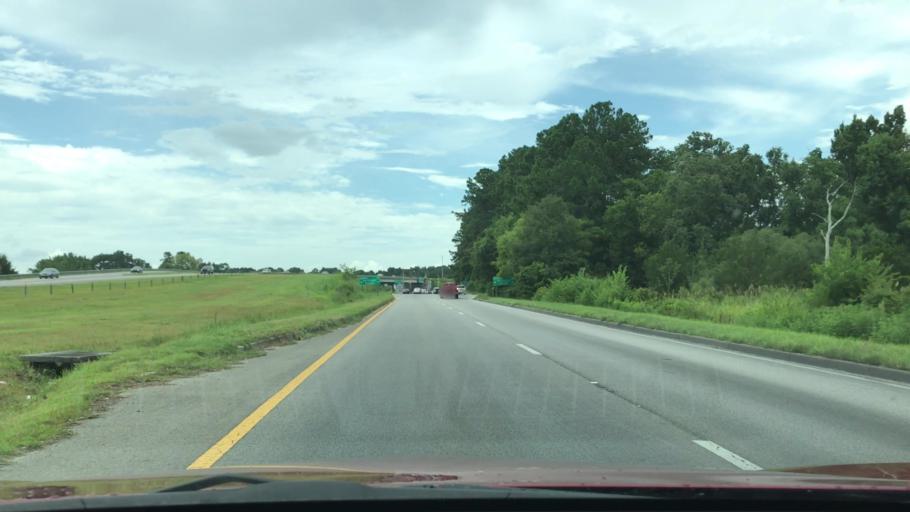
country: US
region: South Carolina
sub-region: Charleston County
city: Shell Point
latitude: 32.7942
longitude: -80.0338
